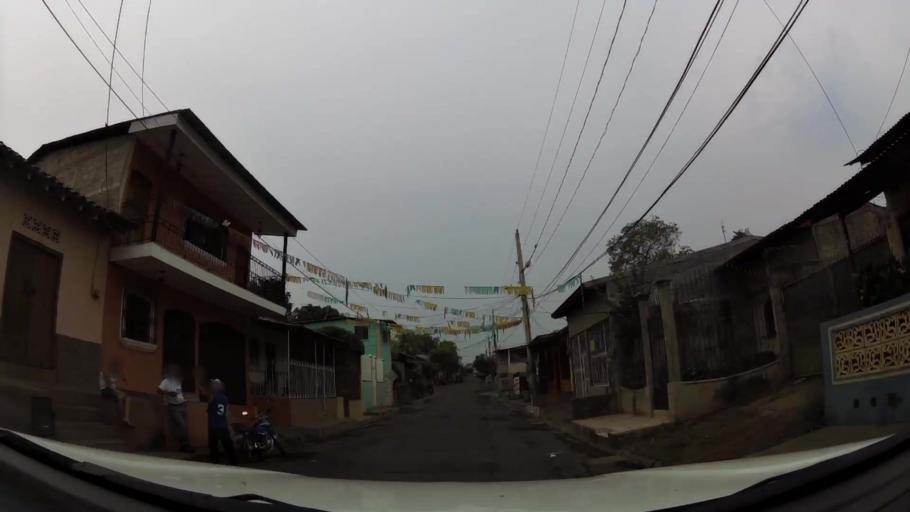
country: NI
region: Leon
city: Leon
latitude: 12.4290
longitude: -86.8801
